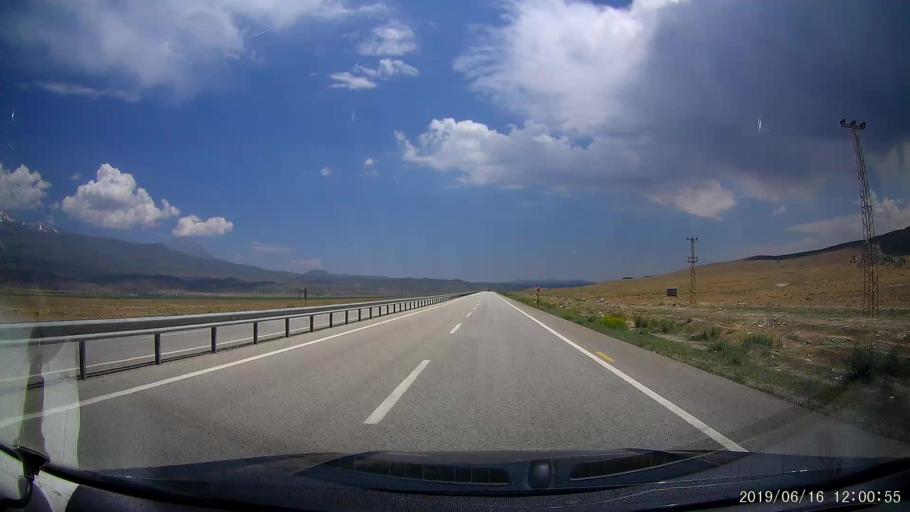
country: TR
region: Agri
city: Dogubayazit
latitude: 39.5560
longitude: 44.1797
